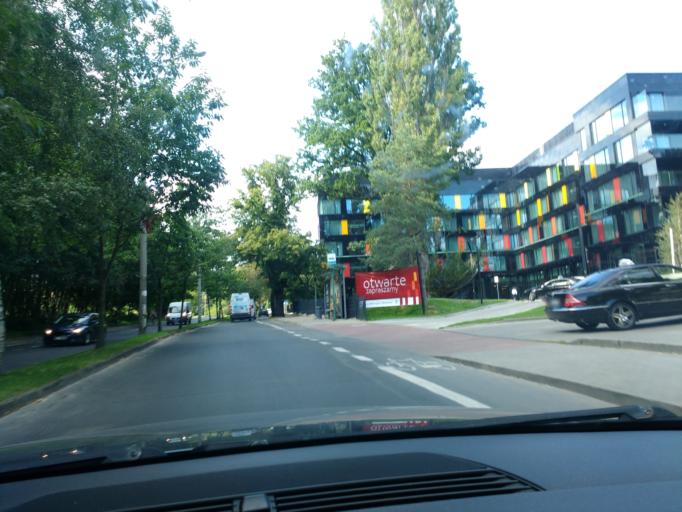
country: PL
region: Pomeranian Voivodeship
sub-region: Sopot
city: Sopot
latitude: 54.4545
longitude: 18.5599
